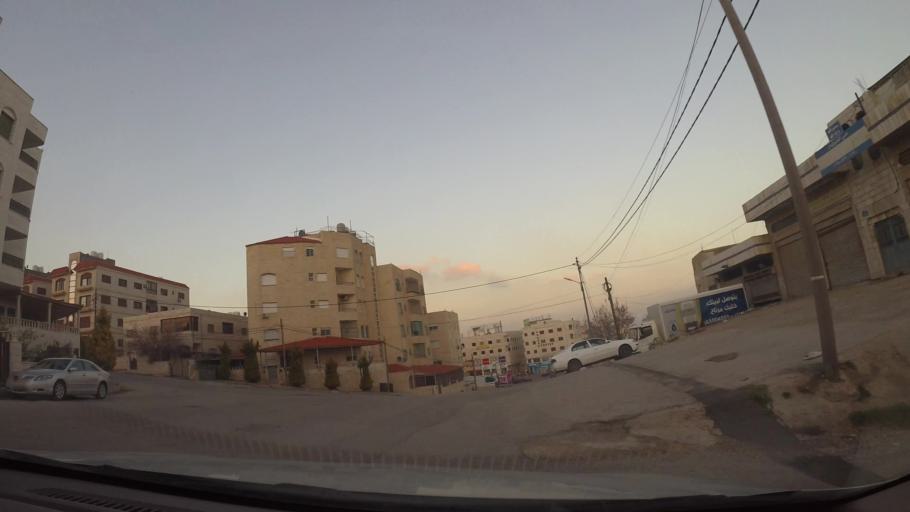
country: JO
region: Amman
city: Al Quwaysimah
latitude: 31.8985
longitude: 35.9319
